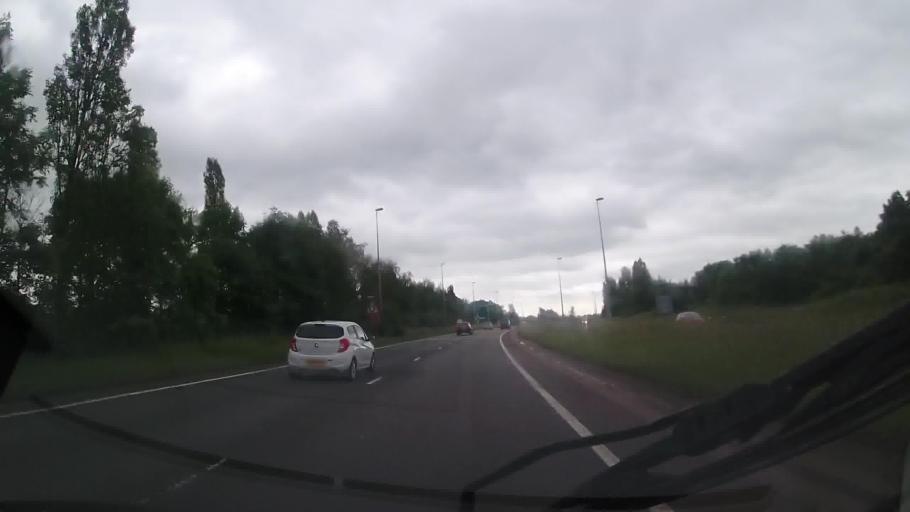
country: GB
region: England
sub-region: Staffordshire
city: Uttoxeter
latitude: 52.9103
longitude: -1.8597
